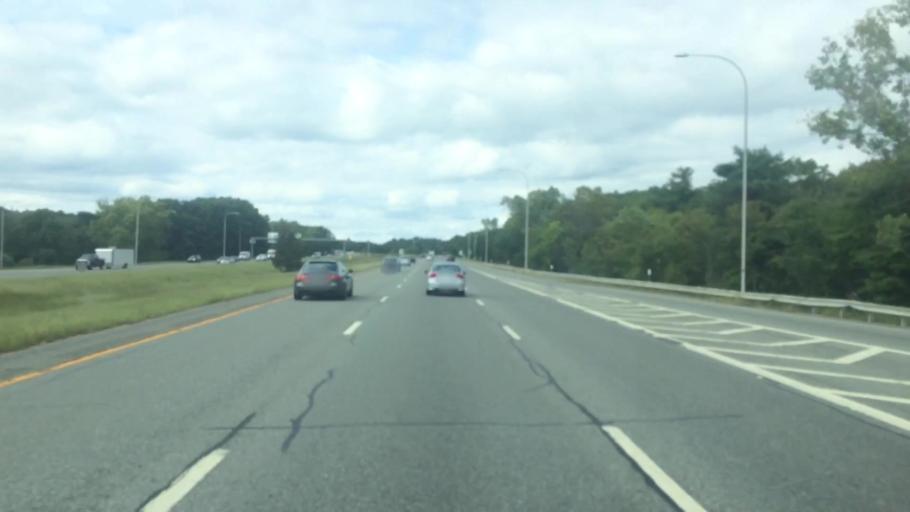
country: US
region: Rhode Island
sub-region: Providence County
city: Greenville
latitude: 41.8718
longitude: -71.5148
